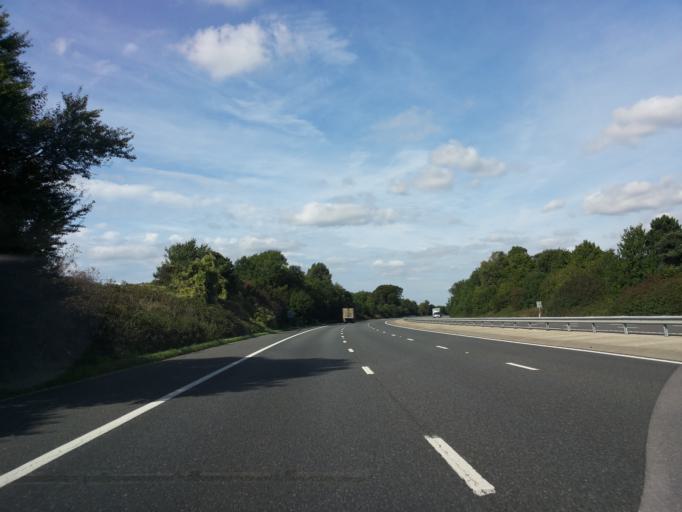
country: GB
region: England
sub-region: Kent
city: Borough Green
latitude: 51.3234
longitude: 0.2761
